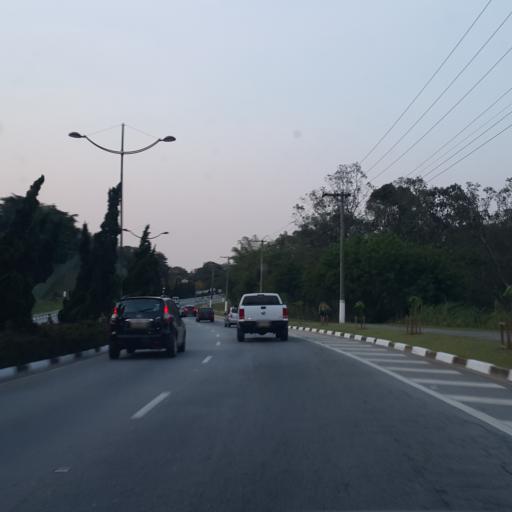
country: BR
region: Sao Paulo
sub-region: Vinhedo
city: Vinhedo
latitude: -23.0517
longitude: -46.9860
